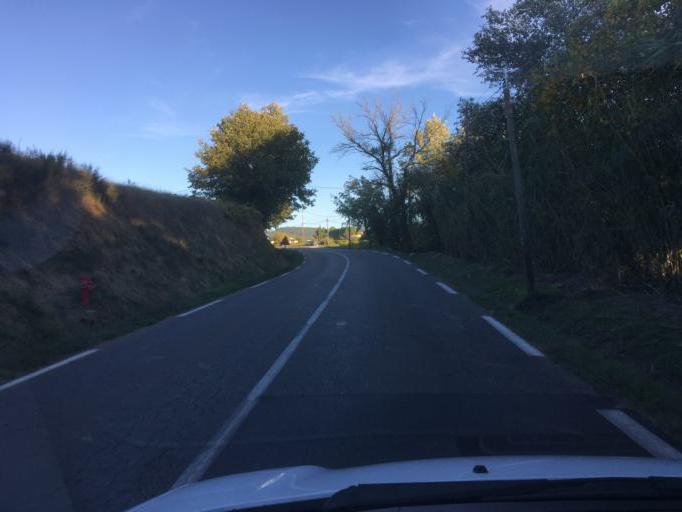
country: FR
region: Provence-Alpes-Cote d'Azur
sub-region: Departement du Vaucluse
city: Mazan
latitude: 44.0594
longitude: 5.1062
